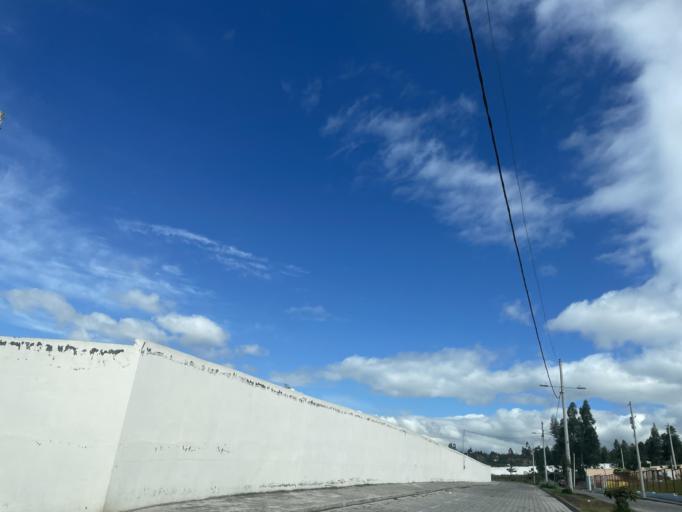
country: EC
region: Chimborazo
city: Guano
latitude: -1.6014
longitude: -78.6426
